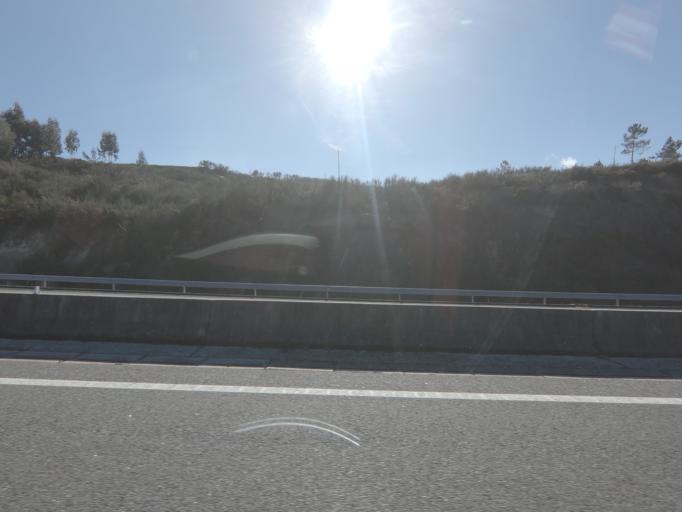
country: ES
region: Galicia
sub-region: Provincia de Pontevedra
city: Dozon
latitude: 42.5650
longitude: -8.0450
